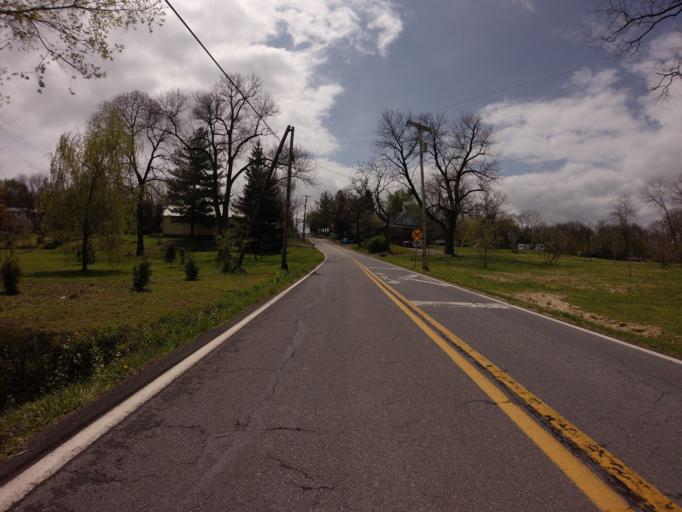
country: US
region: Maryland
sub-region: Frederick County
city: Thurmont
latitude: 39.6074
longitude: -77.3522
